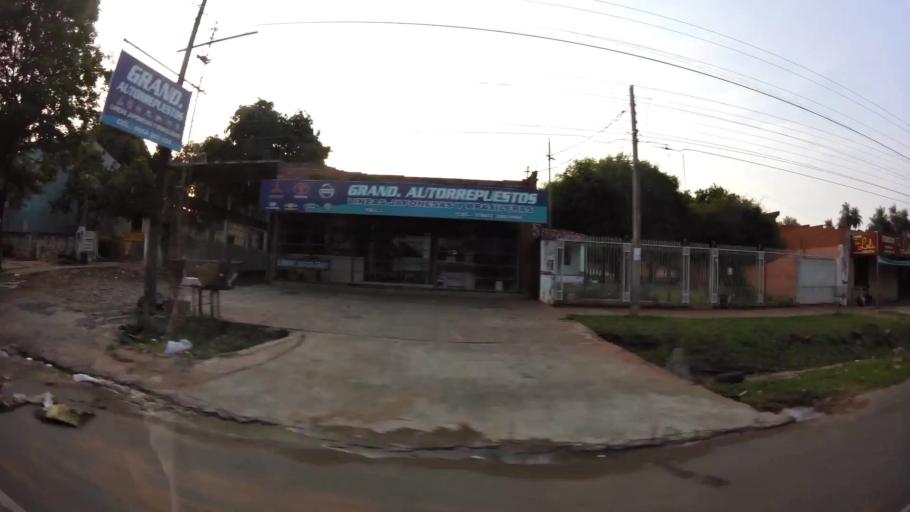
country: PY
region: Central
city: Villa Elisa
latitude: -25.3541
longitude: -57.5935
